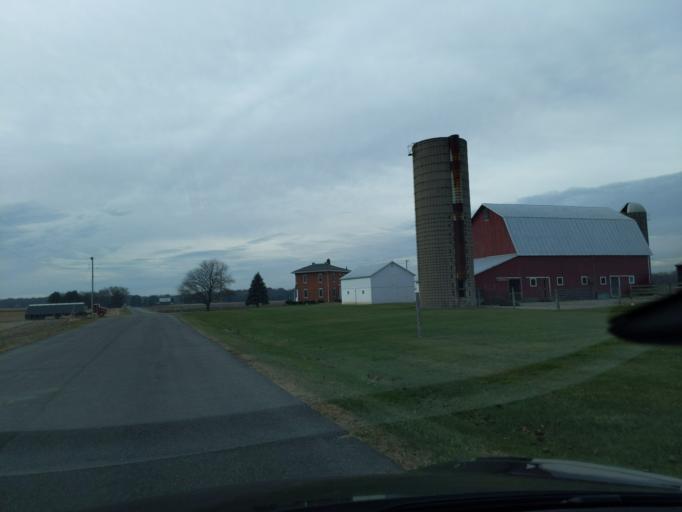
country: US
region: Michigan
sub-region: Ingham County
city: Okemos
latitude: 42.6546
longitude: -84.3818
